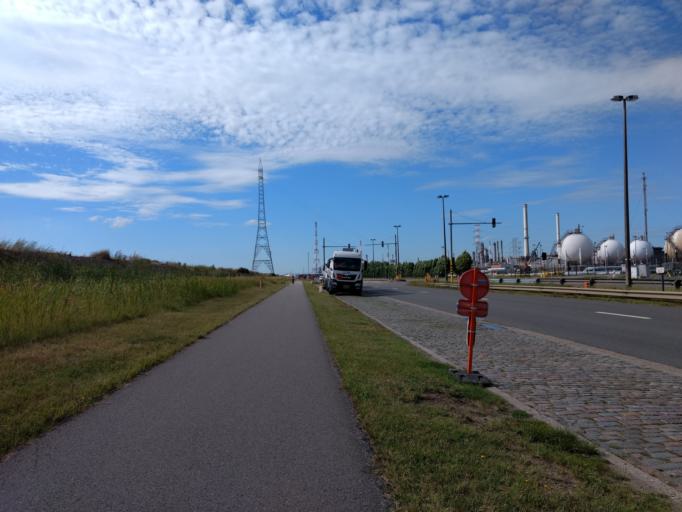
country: BE
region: Flanders
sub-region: Provincie Antwerpen
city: Zwijndrecht
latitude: 51.2460
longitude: 4.3482
